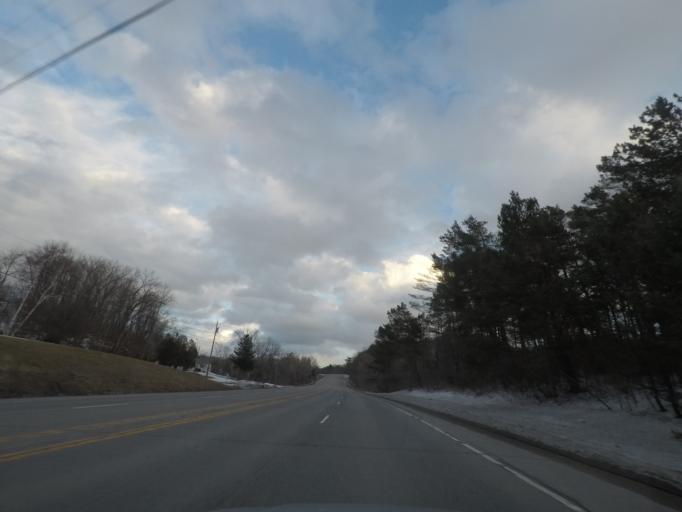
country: US
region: New York
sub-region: Herkimer County
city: Little Falls
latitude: 43.0259
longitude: -74.7909
